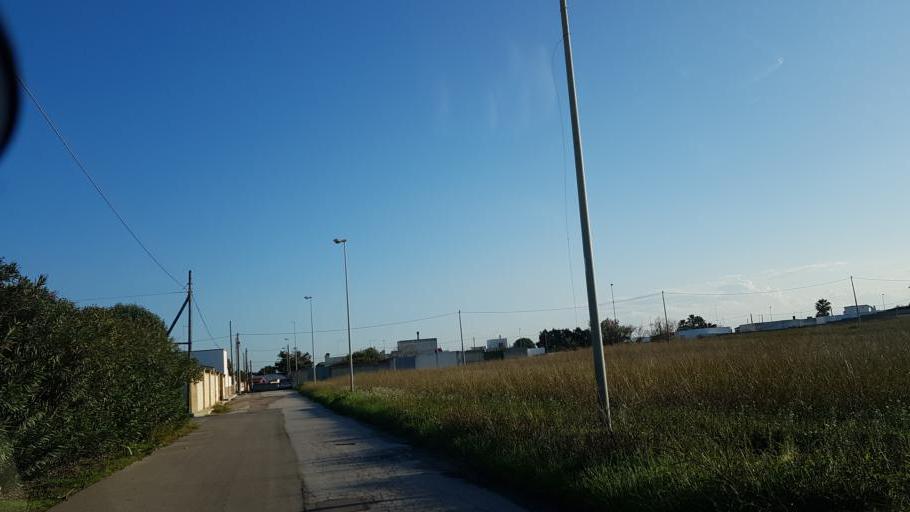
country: IT
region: Apulia
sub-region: Provincia di Brindisi
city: Torchiarolo
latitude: 40.5154
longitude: 18.0943
